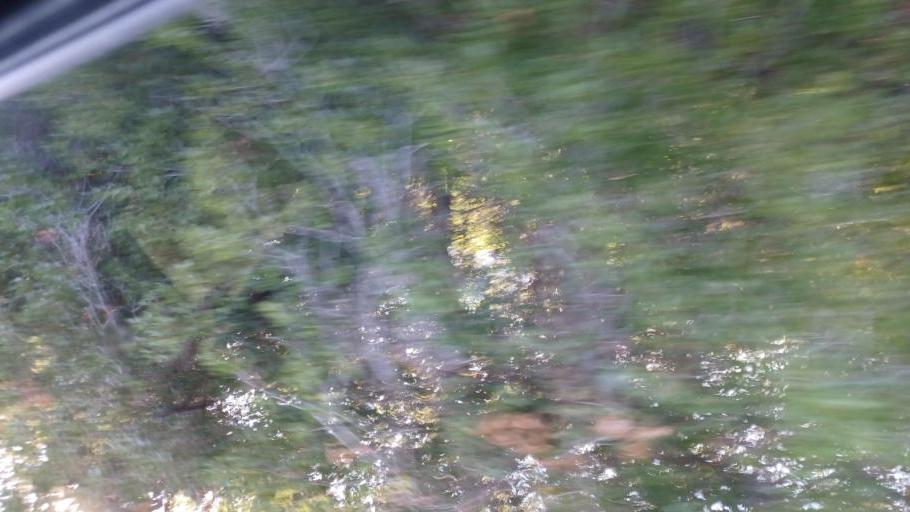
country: CY
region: Pafos
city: Mesogi
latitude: 34.8828
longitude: 32.5198
